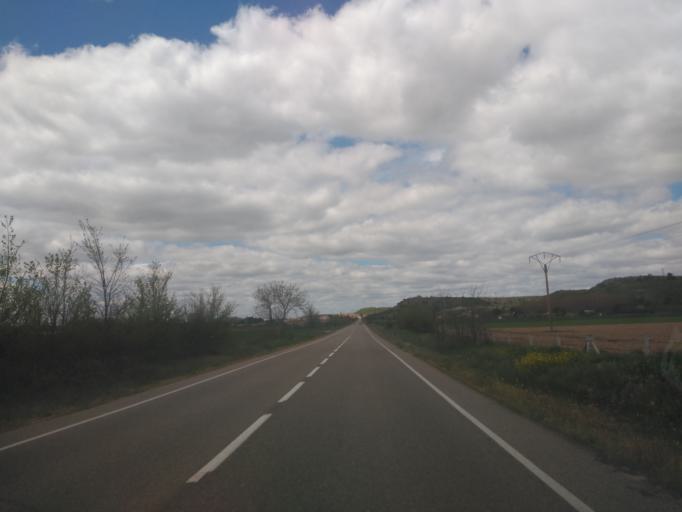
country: ES
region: Castille and Leon
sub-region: Provincia de Salamanca
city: Almenara de Tormes
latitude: 41.0547
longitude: -5.7971
